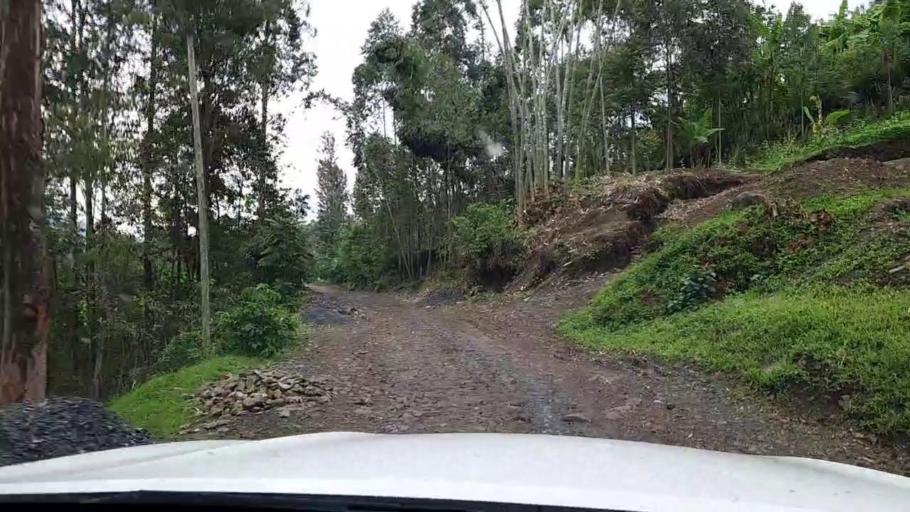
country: RW
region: Western Province
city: Cyangugu
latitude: -2.5435
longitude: 29.0383
